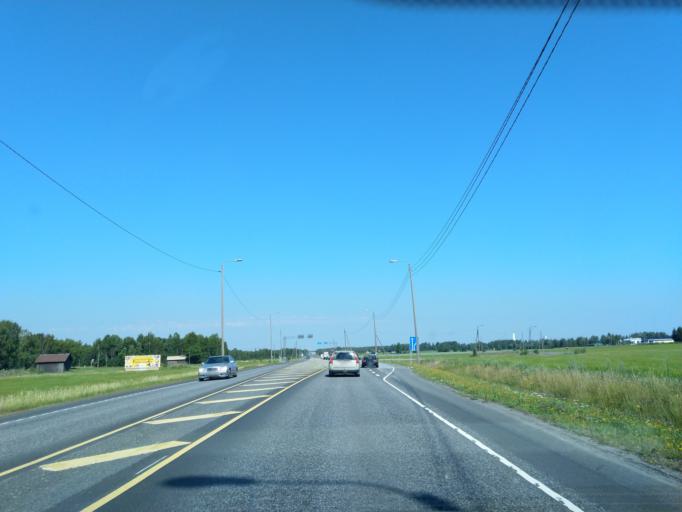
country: FI
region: Satakunta
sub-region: Pori
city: Nakkila
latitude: 61.3490
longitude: 22.0163
